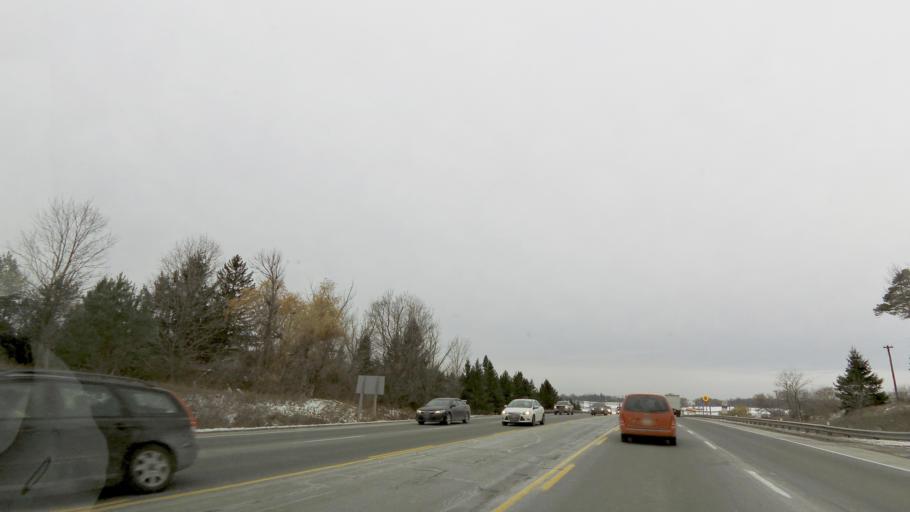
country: CA
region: Ontario
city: Bradford West Gwillimbury
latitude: 44.0335
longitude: -79.5754
